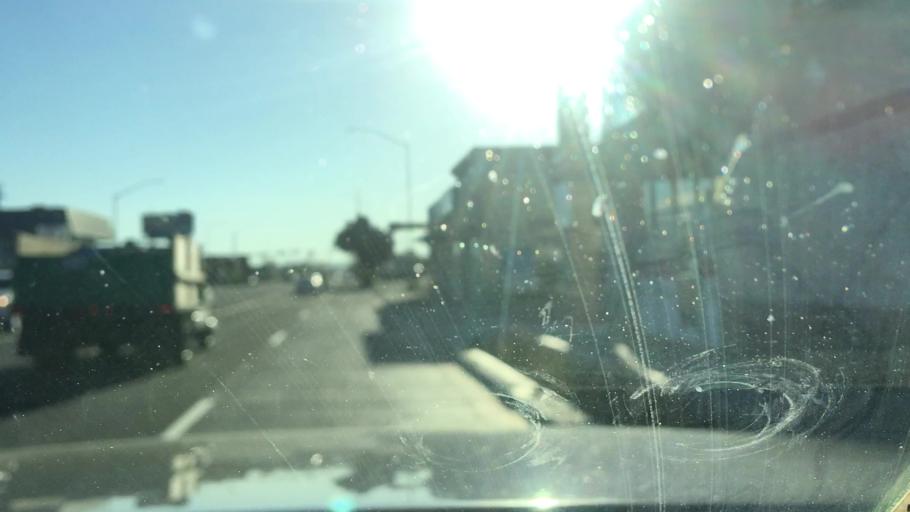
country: US
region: Oregon
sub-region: Lane County
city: Eugene
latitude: 44.0479
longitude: -123.1254
